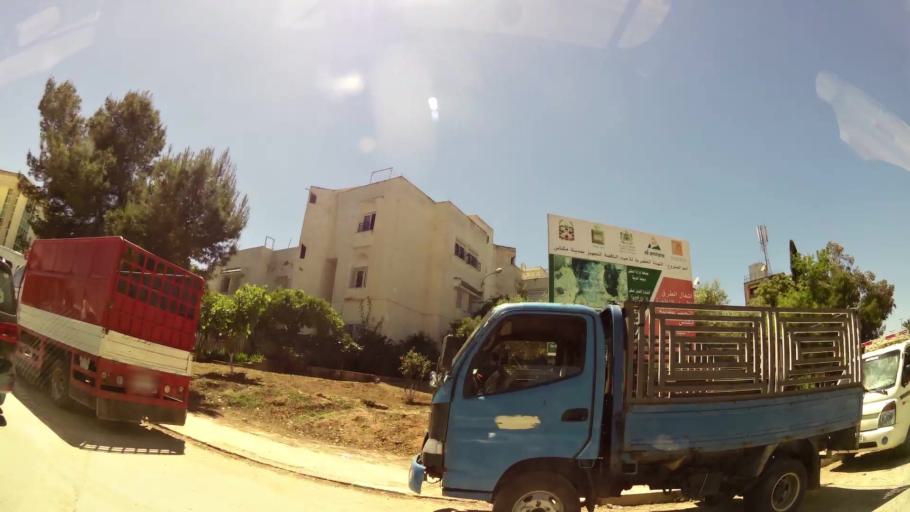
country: MA
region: Meknes-Tafilalet
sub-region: Meknes
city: Meknes
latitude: 33.8962
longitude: -5.5758
